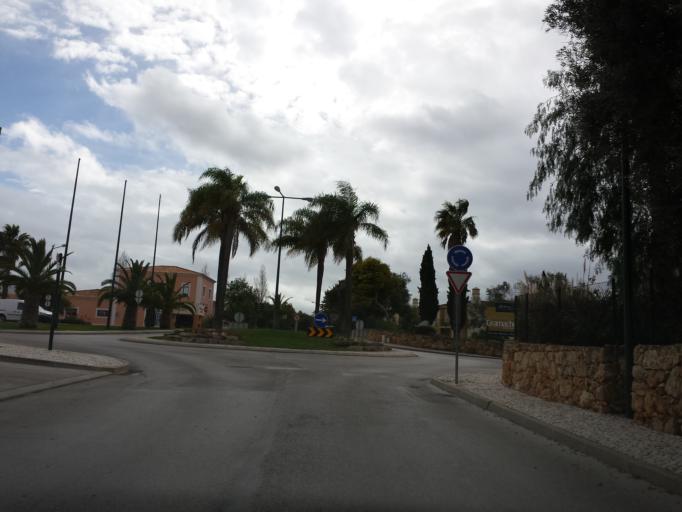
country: PT
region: Faro
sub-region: Lagoa
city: Estombar
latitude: 37.1252
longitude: -8.4855
